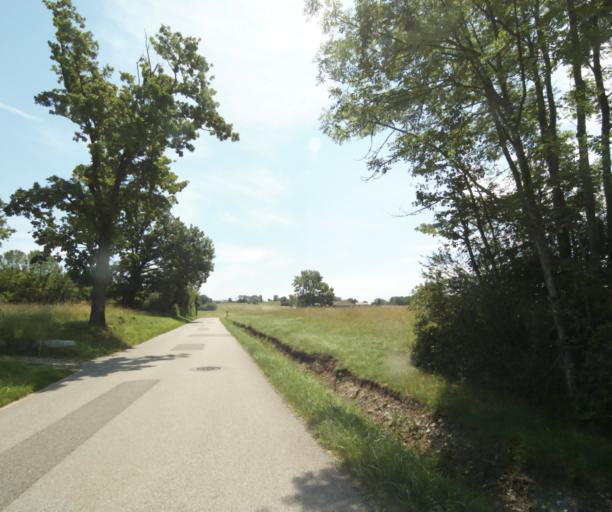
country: FR
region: Rhone-Alpes
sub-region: Departement de la Haute-Savoie
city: Messery
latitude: 46.3621
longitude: 6.3109
